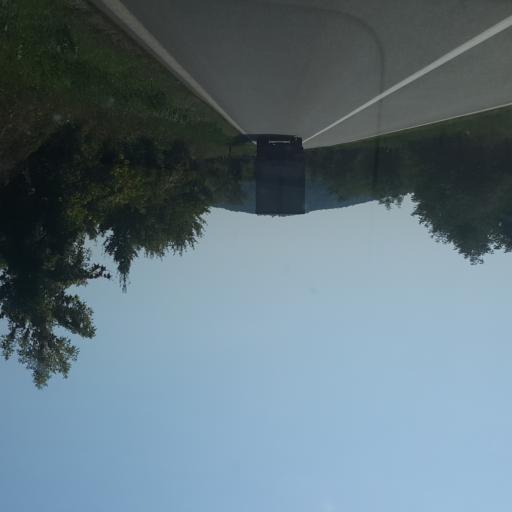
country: RS
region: Central Serbia
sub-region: Zajecarski Okrug
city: Zajecar
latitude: 43.8220
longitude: 22.2876
